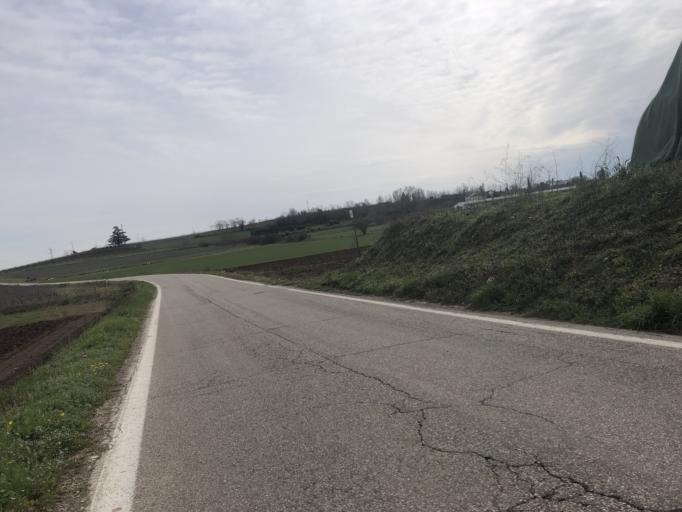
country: IT
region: Veneto
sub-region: Provincia di Verona
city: San Giorgio in Salici
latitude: 45.4344
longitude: 10.8069
